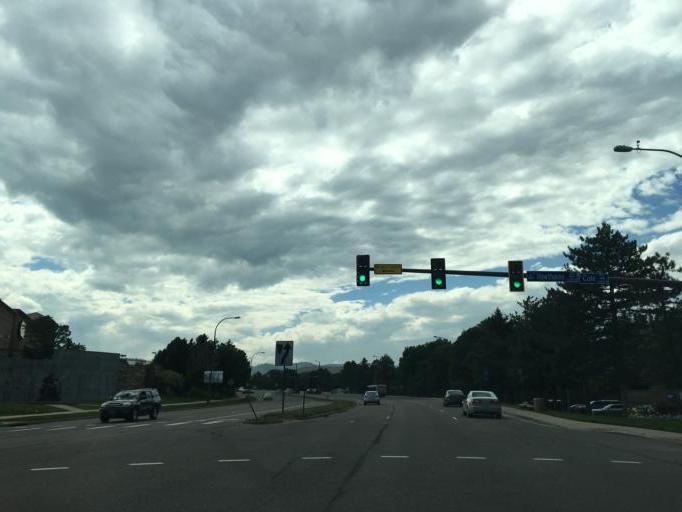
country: US
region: Colorado
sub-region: Jefferson County
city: Applewood
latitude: 39.7385
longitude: -105.1532
